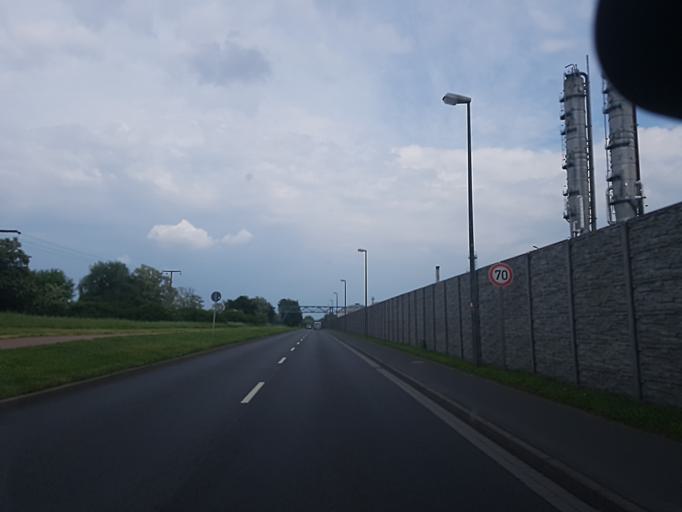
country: DE
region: Saxony-Anhalt
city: Nudersdorf
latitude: 51.8820
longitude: 12.5791
